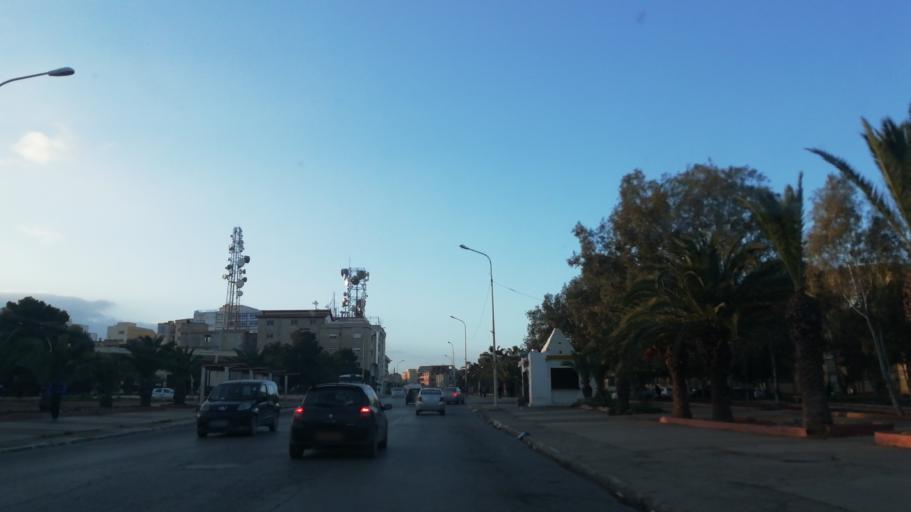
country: DZ
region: Oran
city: Oran
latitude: 35.6707
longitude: -0.6586
